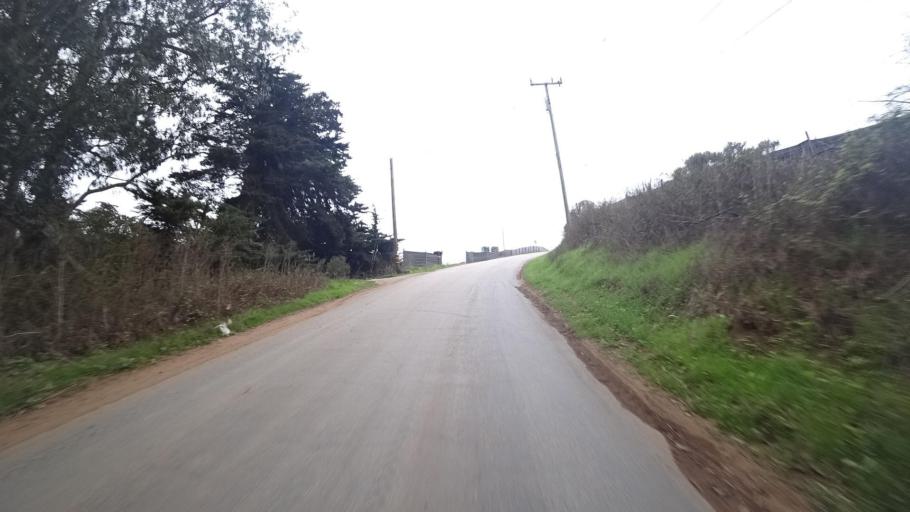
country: US
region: California
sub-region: Monterey County
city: Las Lomas
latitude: 36.8593
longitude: -121.7932
